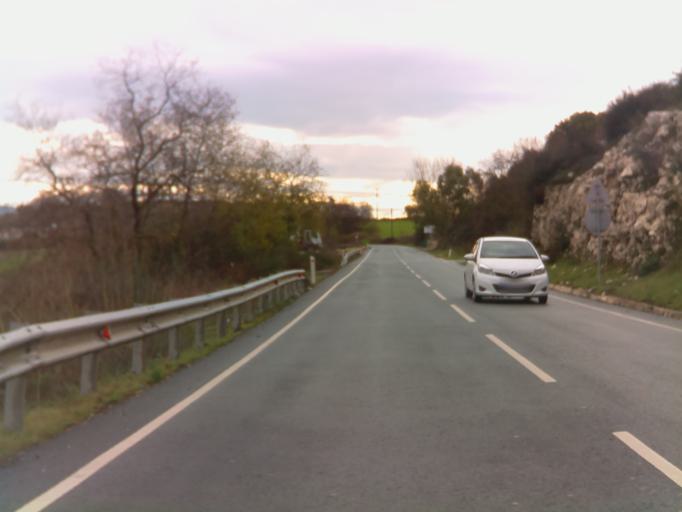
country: CY
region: Pafos
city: Tala
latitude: 34.8930
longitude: 32.4684
